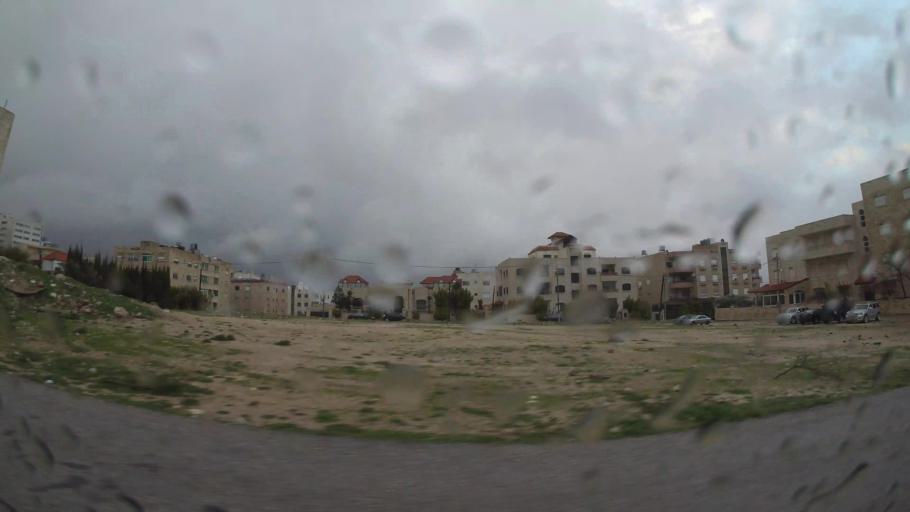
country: JO
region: Amman
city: Amman
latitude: 31.9980
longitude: 35.9205
